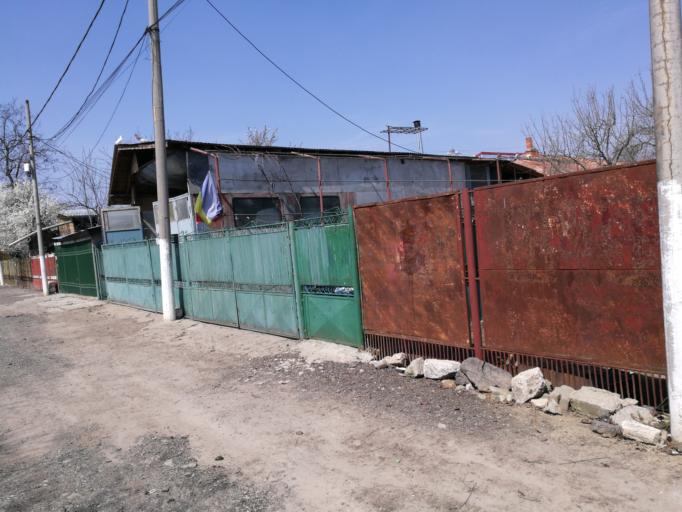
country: RO
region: Ilfov
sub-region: Comuna Chiajna
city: Rosu
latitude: 44.4770
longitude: 26.0277
